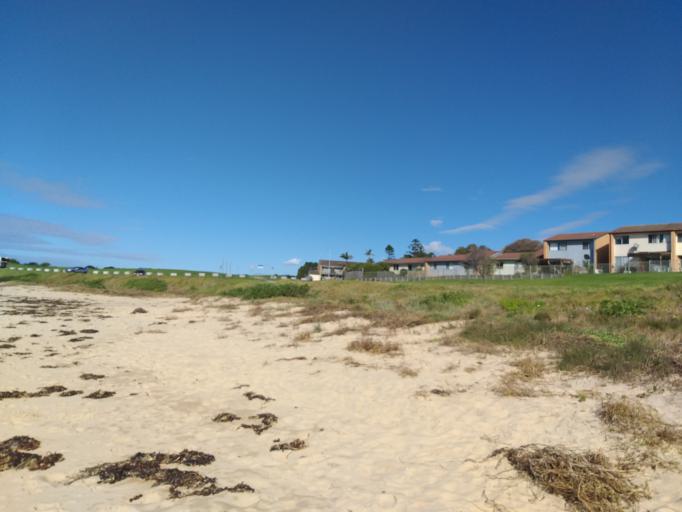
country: AU
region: New South Wales
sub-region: Wollongong
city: East Corrimal
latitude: -34.3665
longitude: 150.9244
